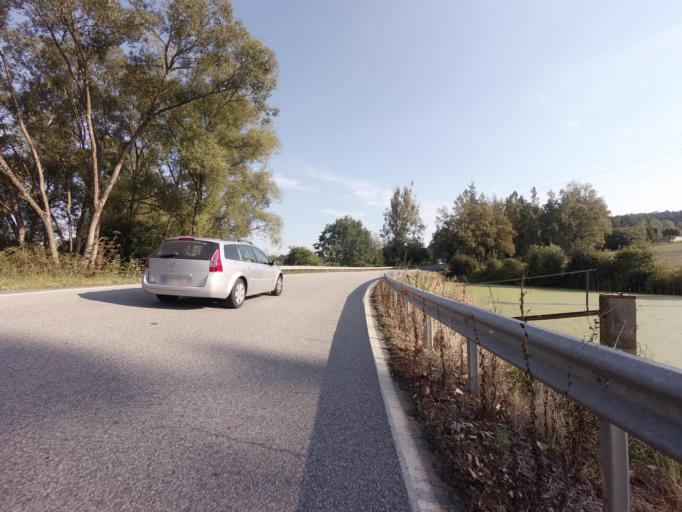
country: CZ
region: Jihocesky
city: Tyn nad Vltavou
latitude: 49.2473
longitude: 14.4198
